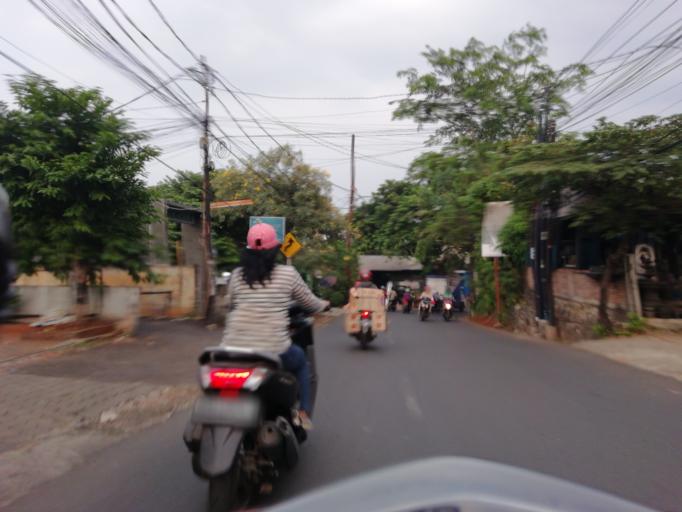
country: ID
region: West Java
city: Depok
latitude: -6.3274
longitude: 106.8172
